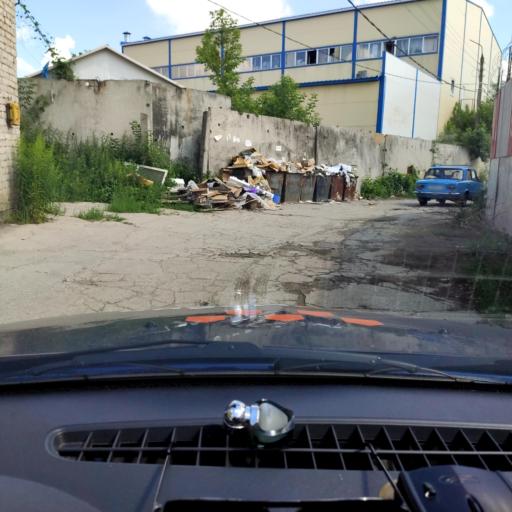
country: RU
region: Orjol
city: Orel
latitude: 52.9831
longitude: 36.0393
